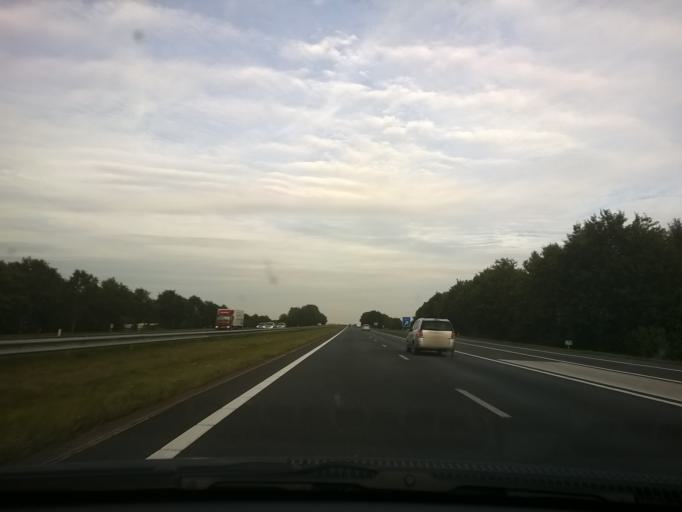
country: NL
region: Groningen
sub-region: Gemeente Grootegast
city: Grootegast
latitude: 53.1515
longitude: 6.2630
